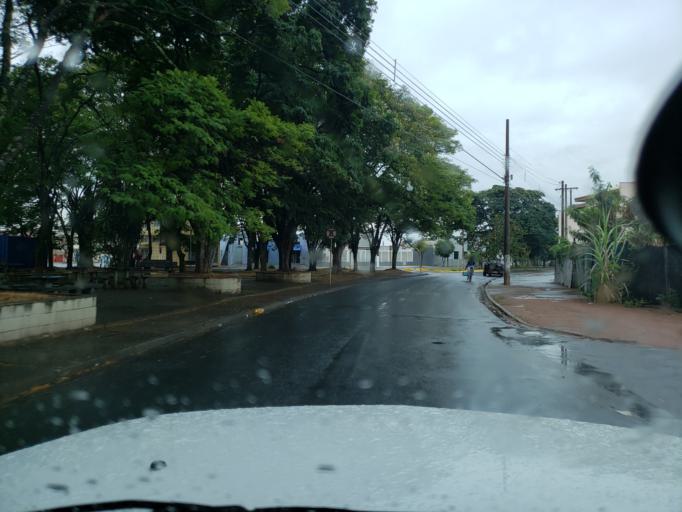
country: BR
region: Sao Paulo
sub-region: Moji-Guacu
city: Mogi-Gaucu
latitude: -22.3528
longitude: -46.9433
